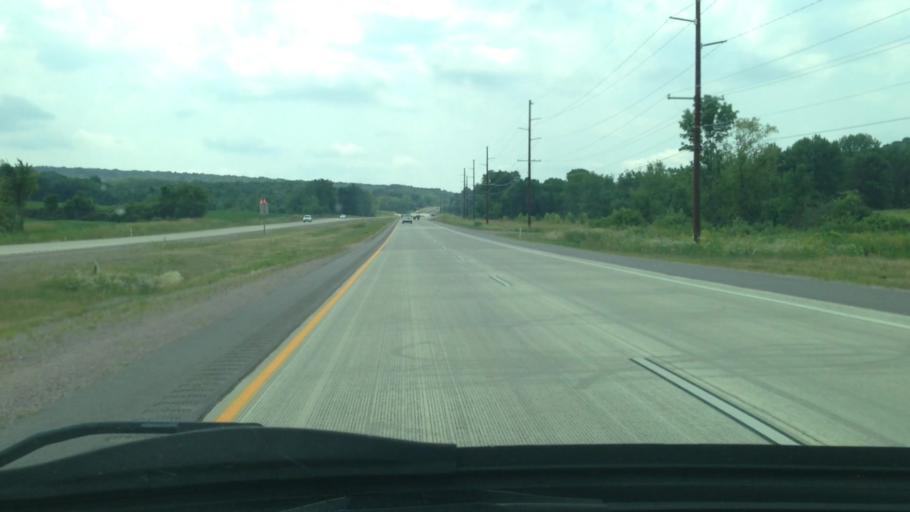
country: US
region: Wisconsin
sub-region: Sauk County
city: West Baraboo
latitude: 43.4186
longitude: -89.7734
